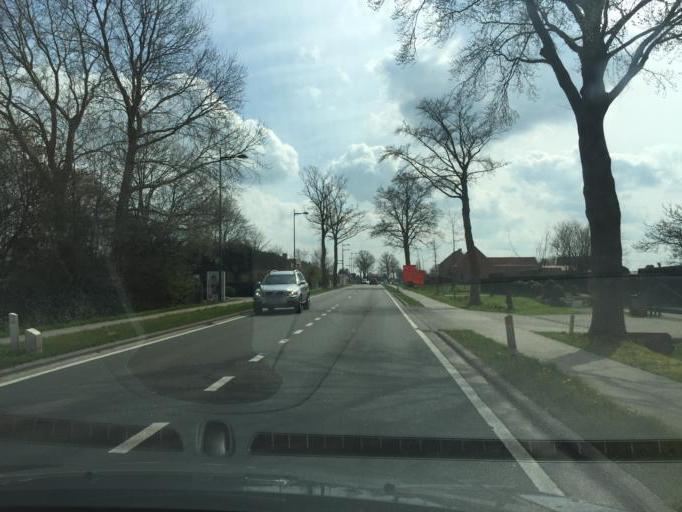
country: BE
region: Flanders
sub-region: Provincie Oost-Vlaanderen
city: Aalter
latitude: 51.0683
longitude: 3.4542
